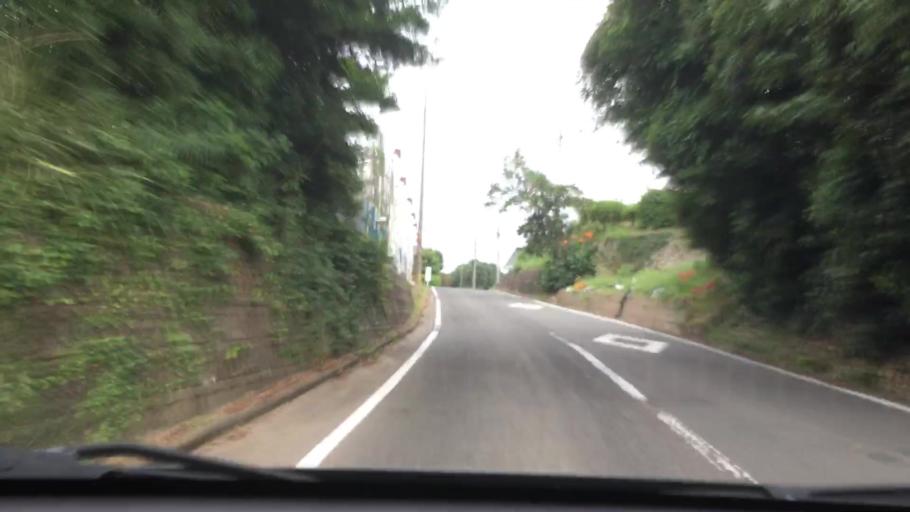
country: JP
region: Nagasaki
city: Sasebo
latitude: 32.9988
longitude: 129.7673
